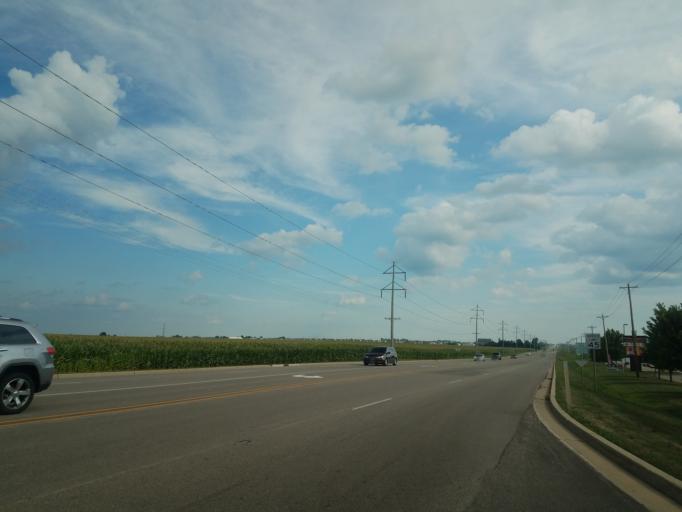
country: US
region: Illinois
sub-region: McLean County
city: Normal
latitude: 40.5025
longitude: -88.9028
